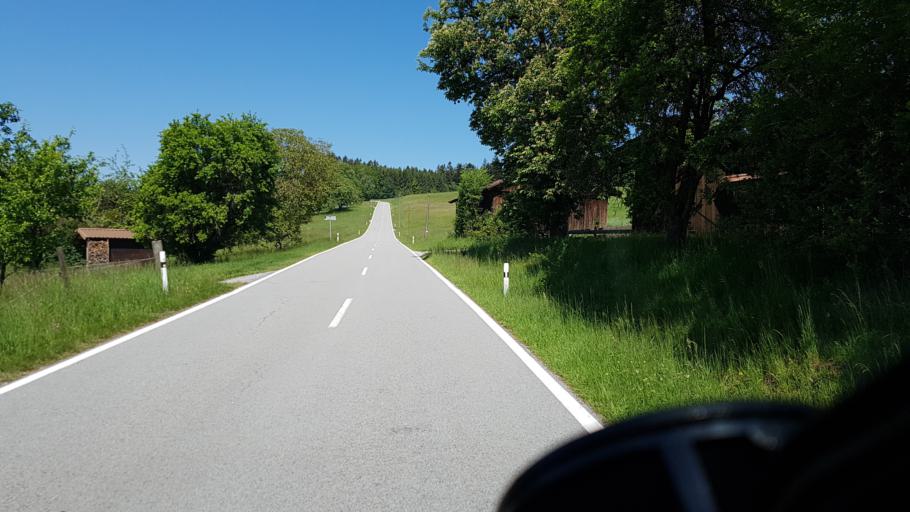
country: DE
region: Bavaria
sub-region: Lower Bavaria
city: Stubenberg
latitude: 48.2986
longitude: 13.0488
